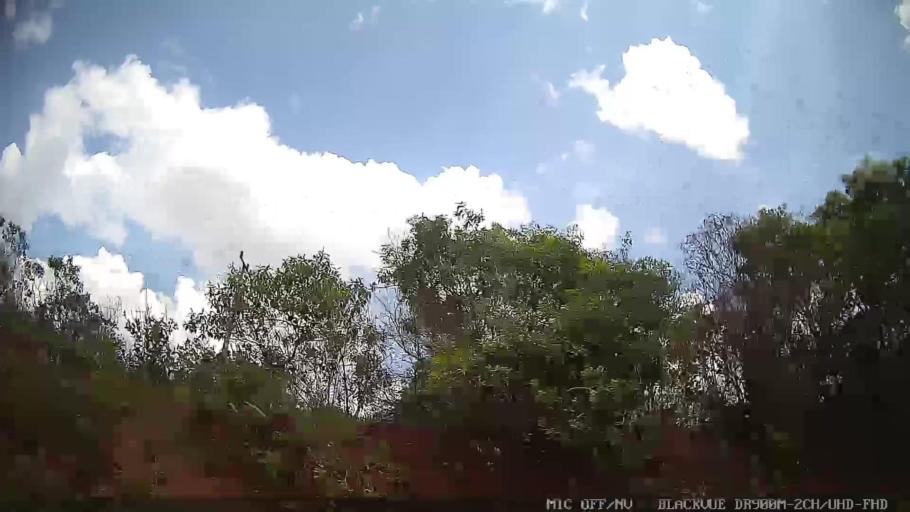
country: BR
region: Sao Paulo
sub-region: Braganca Paulista
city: Braganca Paulista
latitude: -22.9502
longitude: -46.5987
